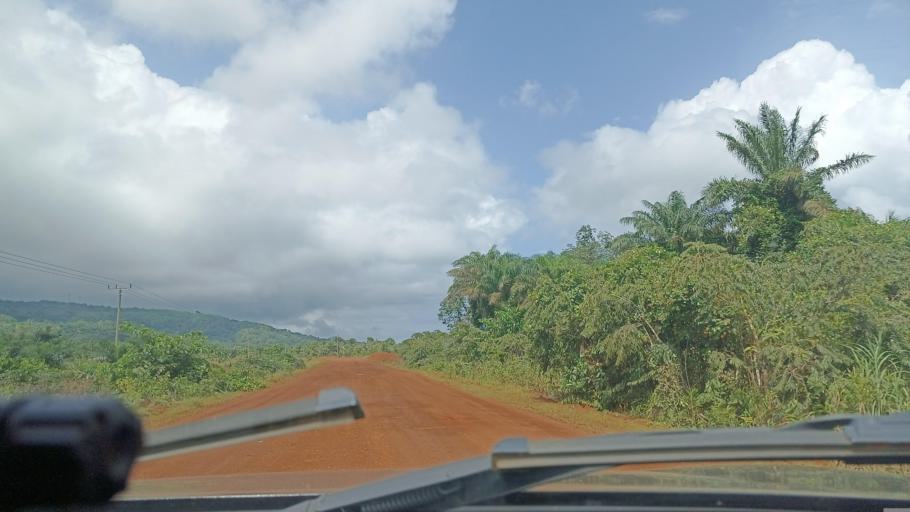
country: LR
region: Grand Cape Mount
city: Robertsport
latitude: 6.7487
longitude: -11.3442
